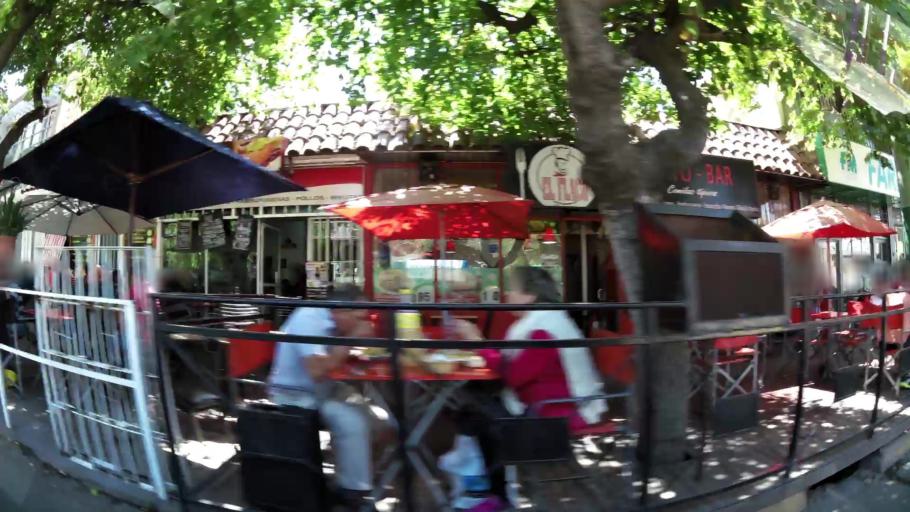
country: AR
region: Mendoza
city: Mendoza
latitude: -32.8939
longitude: -68.8290
